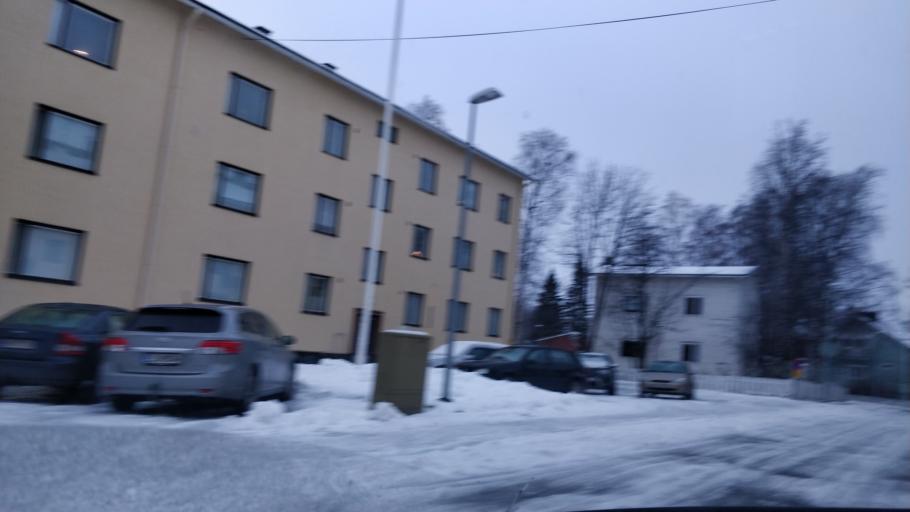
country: FI
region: Lapland
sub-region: Kemi-Tornio
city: Kemi
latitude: 65.7416
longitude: 24.5635
